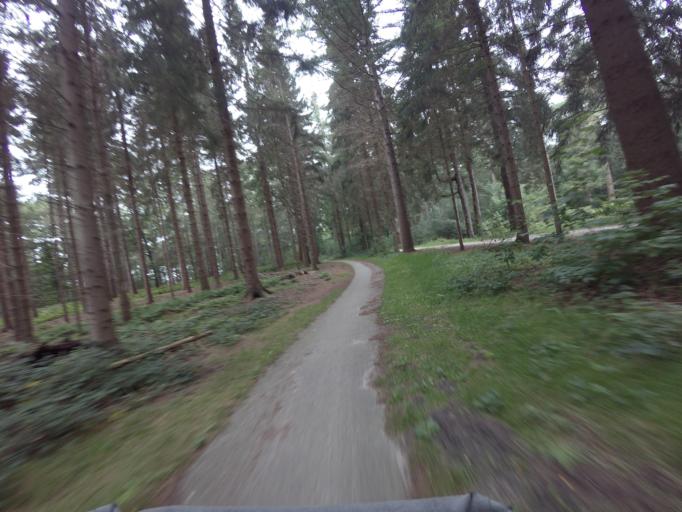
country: NL
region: Overijssel
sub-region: Gemeente Steenwijkerland
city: Tuk
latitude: 52.8241
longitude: 6.1000
